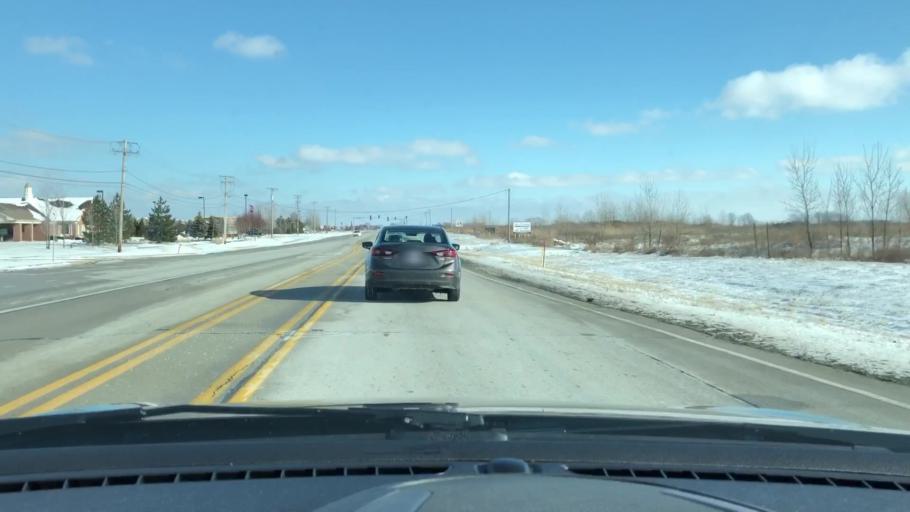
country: US
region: Illinois
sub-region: Will County
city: New Lenox
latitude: 41.4837
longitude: -87.9257
